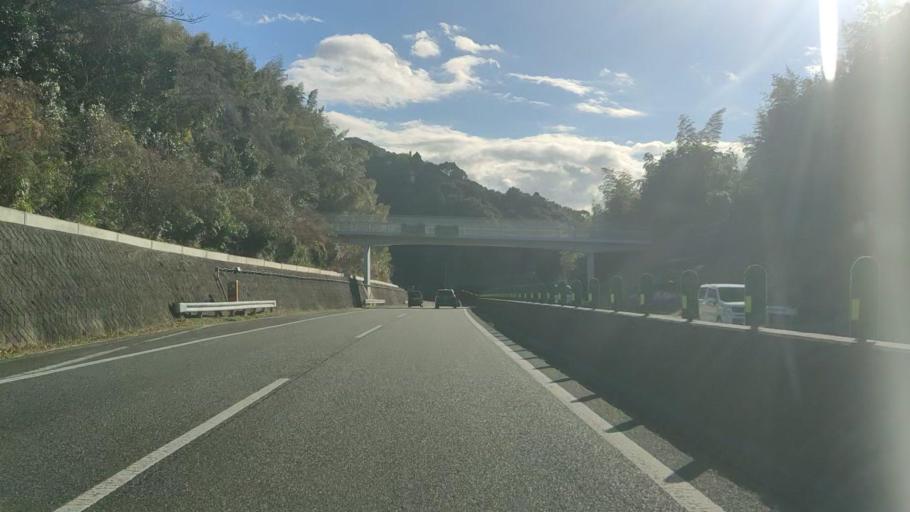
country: JP
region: Fukuoka
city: Kitakyushu
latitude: 33.8340
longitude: 130.7658
